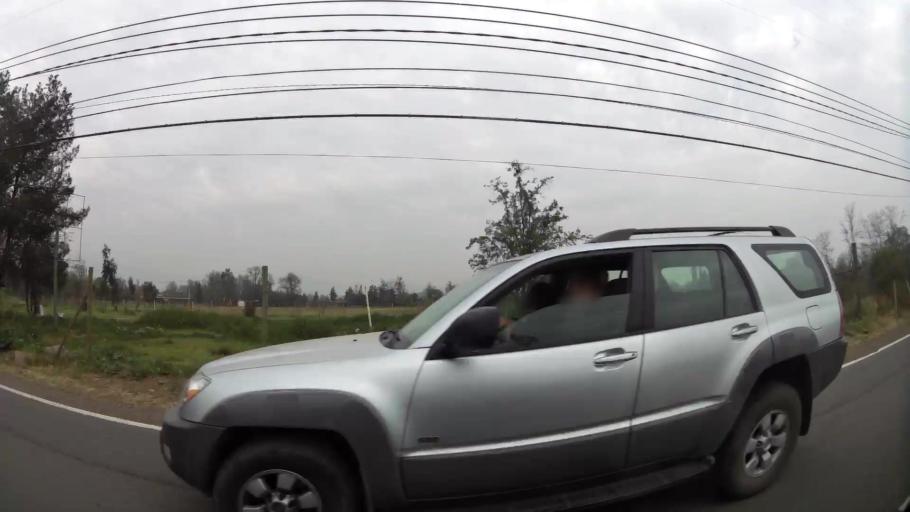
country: CL
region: Santiago Metropolitan
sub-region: Provincia de Chacabuco
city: Chicureo Abajo
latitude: -33.2084
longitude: -70.6632
